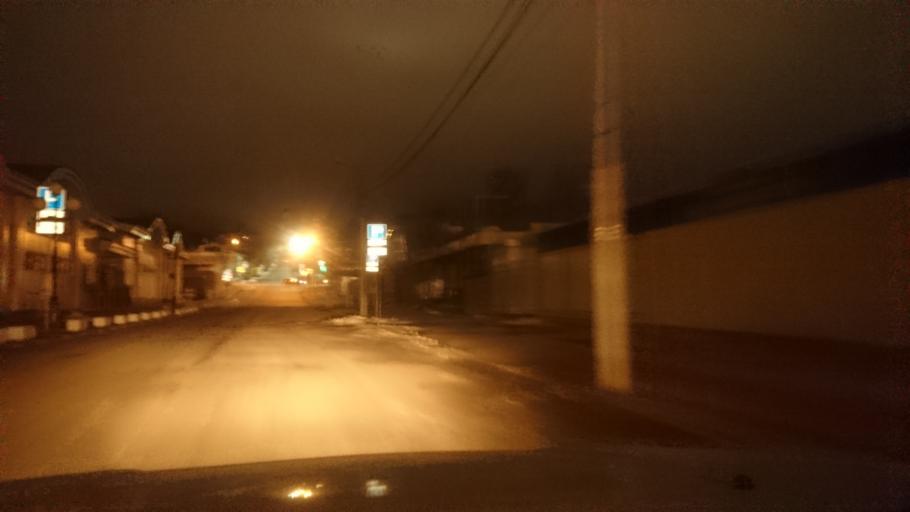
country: RU
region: Tula
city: Tula
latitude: 54.1866
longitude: 37.6183
